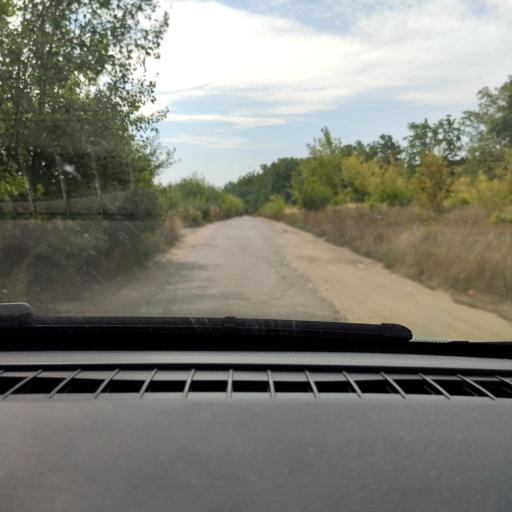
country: RU
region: Voronezj
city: Pridonskoy
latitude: 51.7476
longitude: 39.0749
